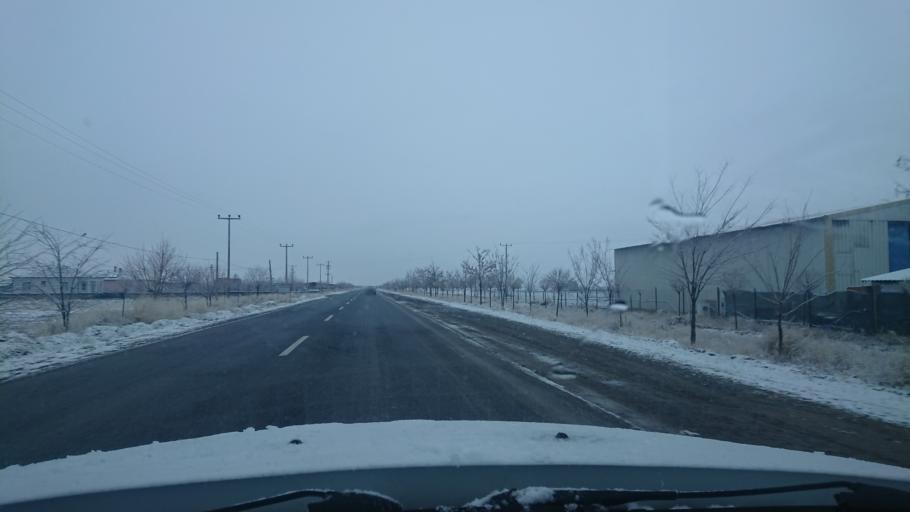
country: TR
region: Aksaray
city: Yesilova
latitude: 38.2982
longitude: 33.7580
